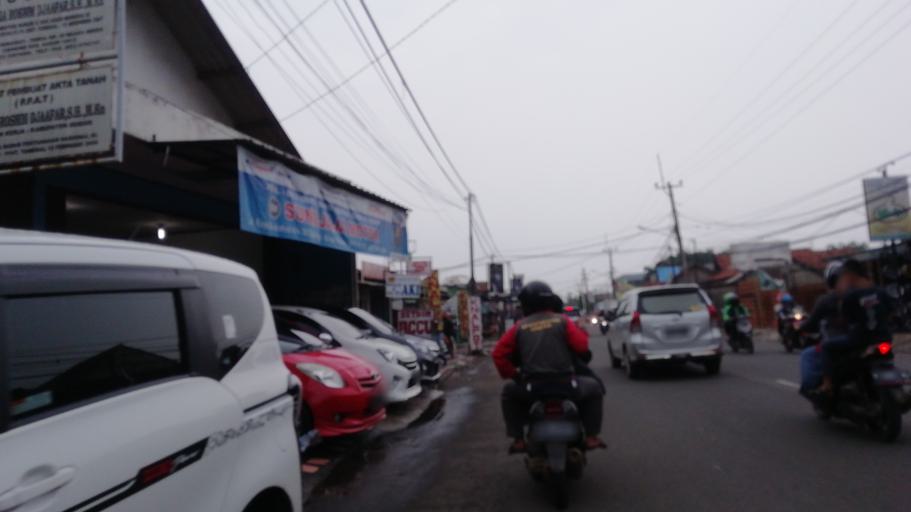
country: ID
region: West Java
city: Cibinong
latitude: -6.5001
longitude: 106.8104
